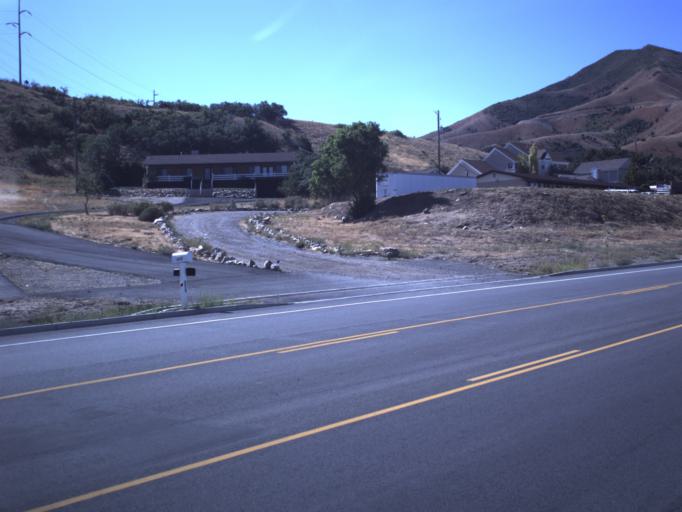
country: US
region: Utah
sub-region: Tooele County
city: Tooele
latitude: 40.5200
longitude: -112.2993
